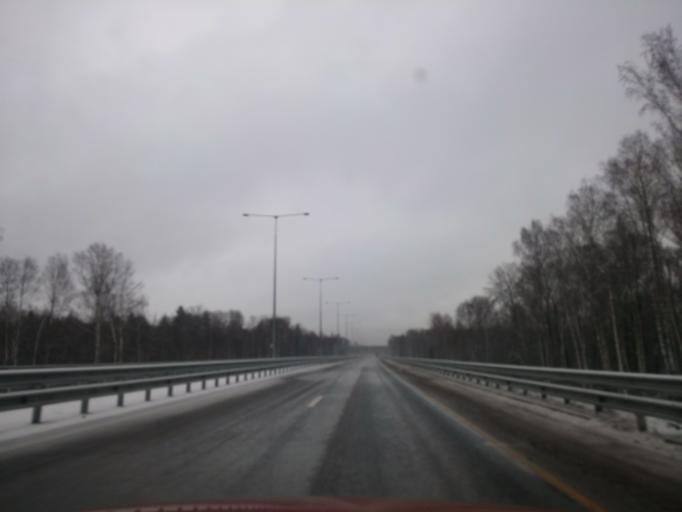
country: RU
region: Tverskaya
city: Likhoslavl'
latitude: 56.9658
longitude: 35.4704
